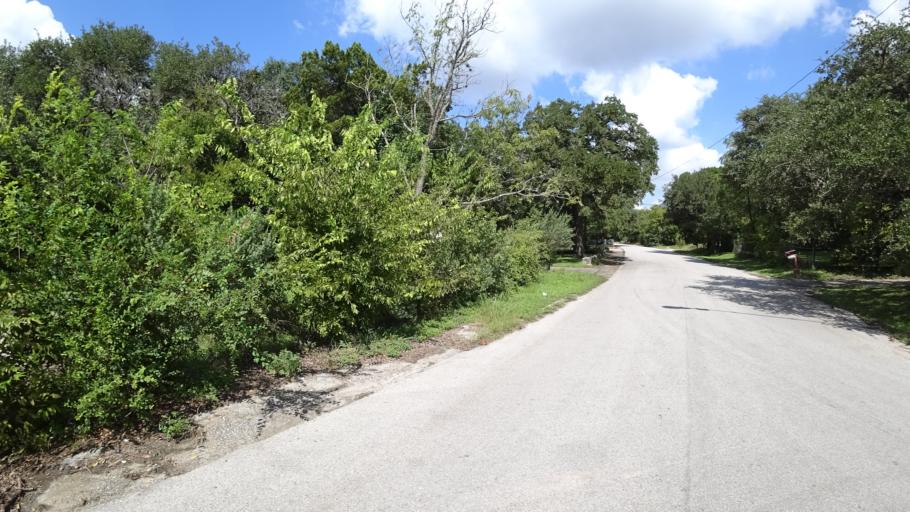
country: US
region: Texas
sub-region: Travis County
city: Onion Creek
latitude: 30.1888
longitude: -97.8031
